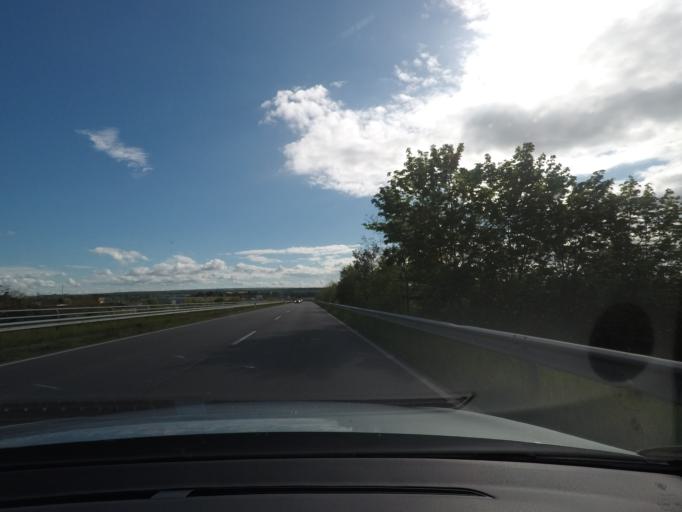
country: DE
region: Lower Saxony
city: Helmstedt
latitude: 52.2457
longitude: 10.9921
